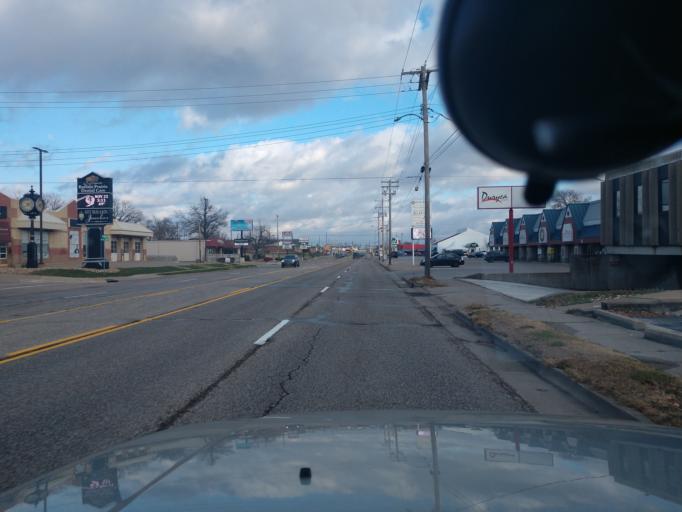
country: US
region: Illinois
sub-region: Adams County
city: Quincy
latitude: 39.9353
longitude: -91.3712
